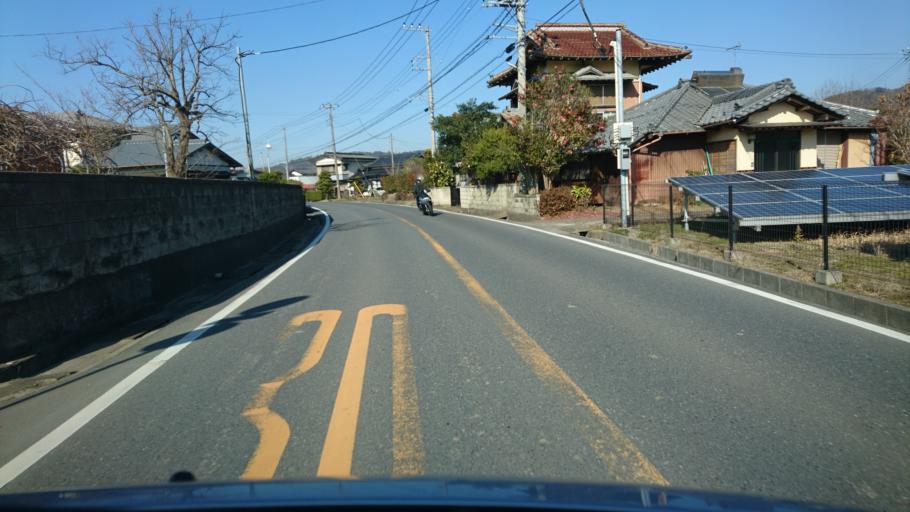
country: JP
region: Chiba
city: Kimitsu
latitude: 35.3003
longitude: 139.9750
